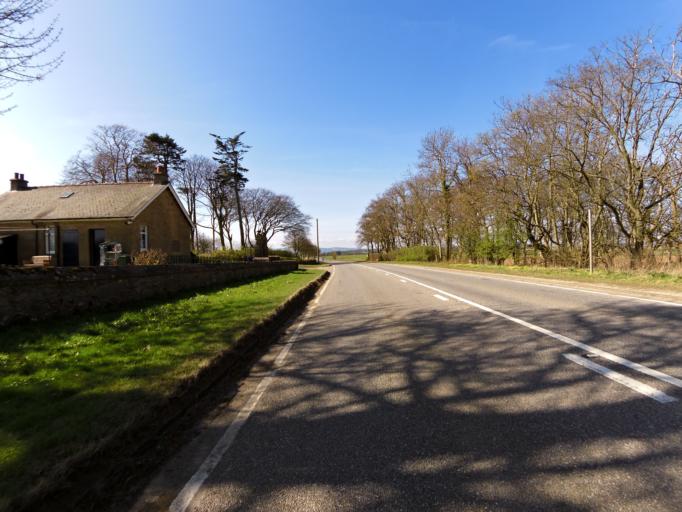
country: GB
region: Scotland
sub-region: Angus
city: Montrose
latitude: 56.7686
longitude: -2.4326
